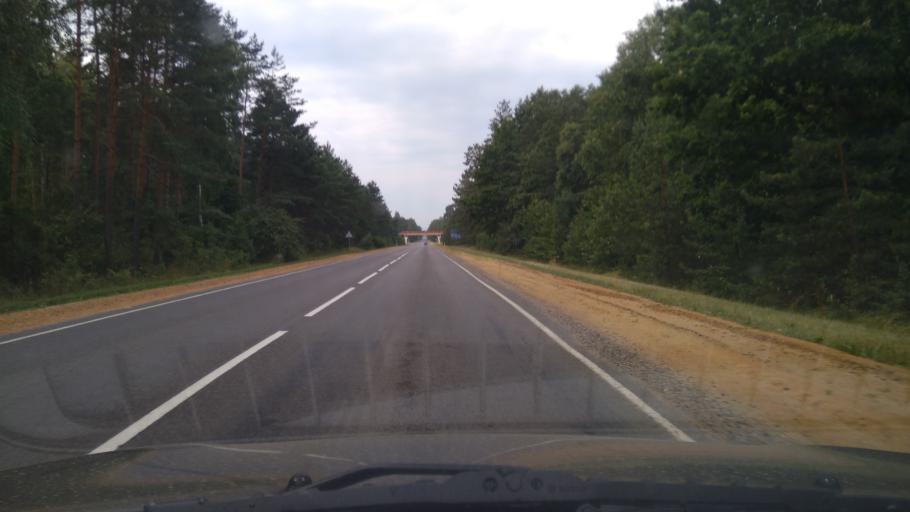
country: BY
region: Brest
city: Nyakhachava
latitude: 52.5910
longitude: 25.0985
